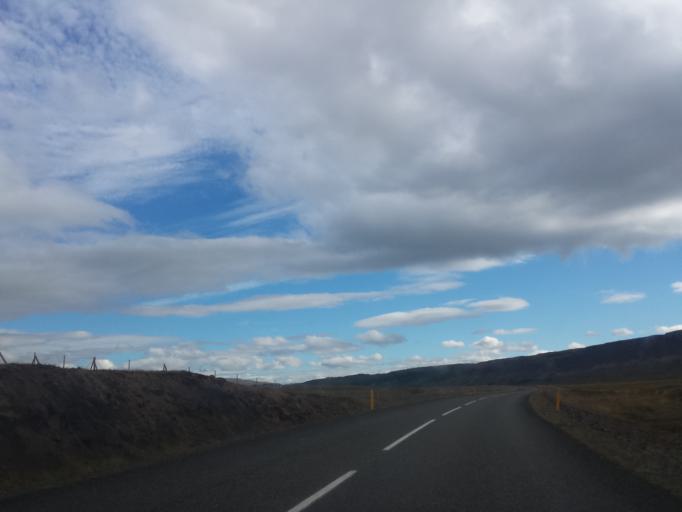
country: IS
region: West
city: Borgarnes
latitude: 64.4231
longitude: -21.7695
